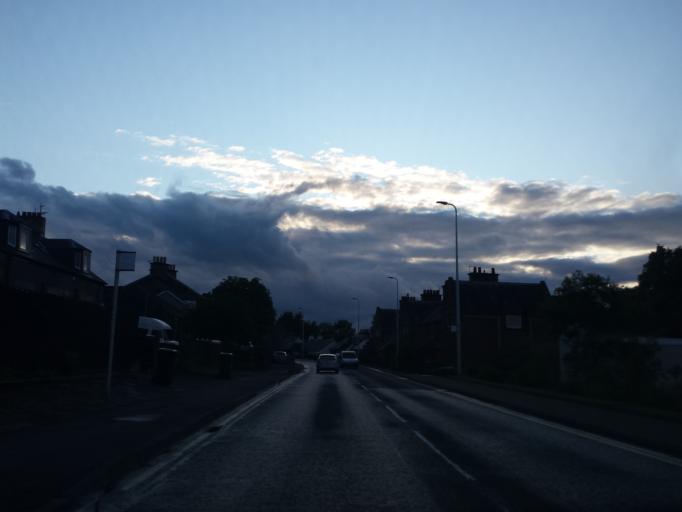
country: GB
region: Scotland
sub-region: Perth and Kinross
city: Perth
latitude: 56.4068
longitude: -3.4648
